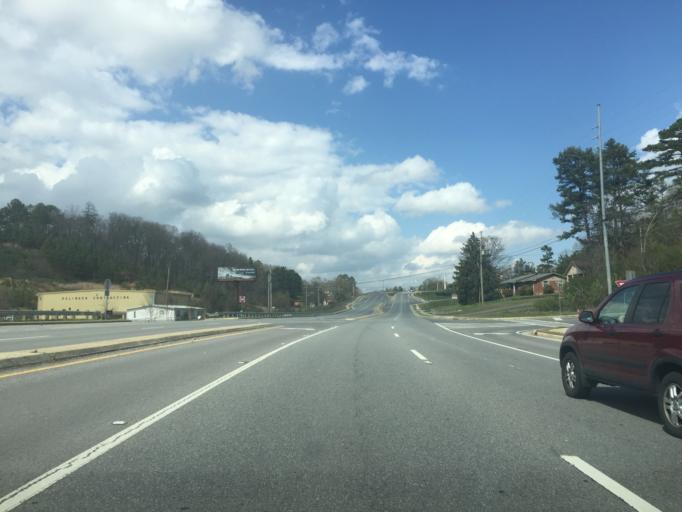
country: US
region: Georgia
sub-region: Catoosa County
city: Indian Springs
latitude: 34.9725
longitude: -85.1910
